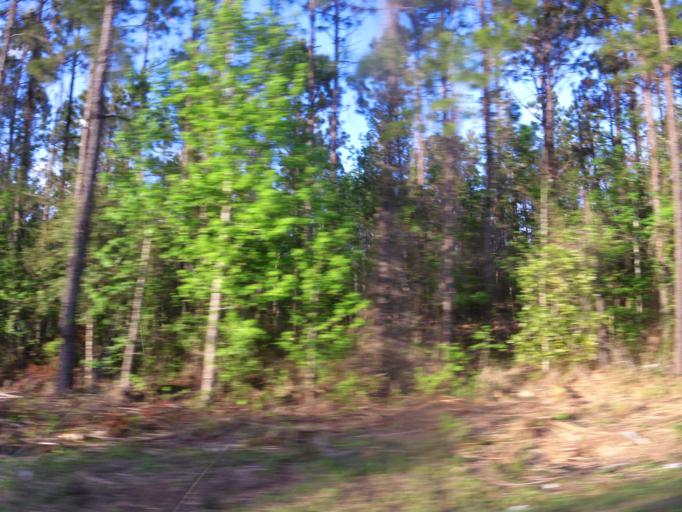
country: US
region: Florida
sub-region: Saint Johns County
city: Fruit Cove
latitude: 30.0784
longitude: -81.5222
